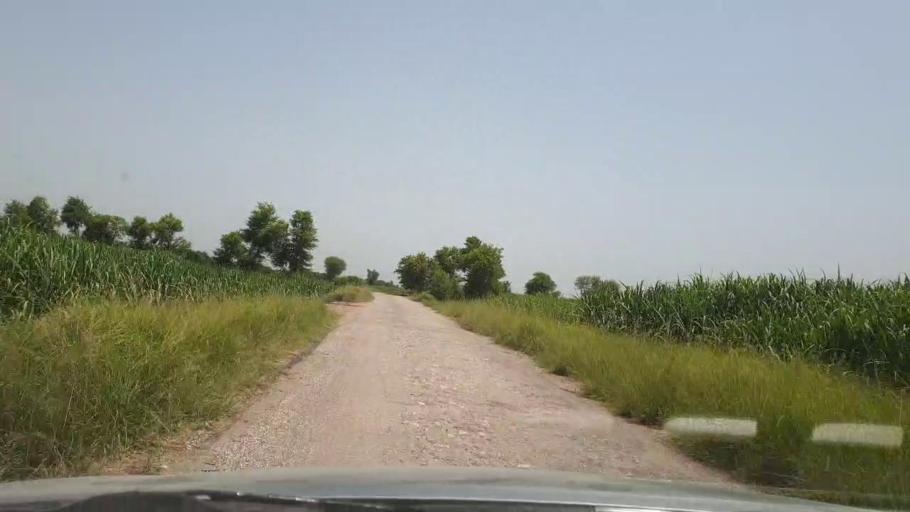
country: PK
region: Sindh
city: Pano Aqil
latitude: 27.8067
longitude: 69.2385
